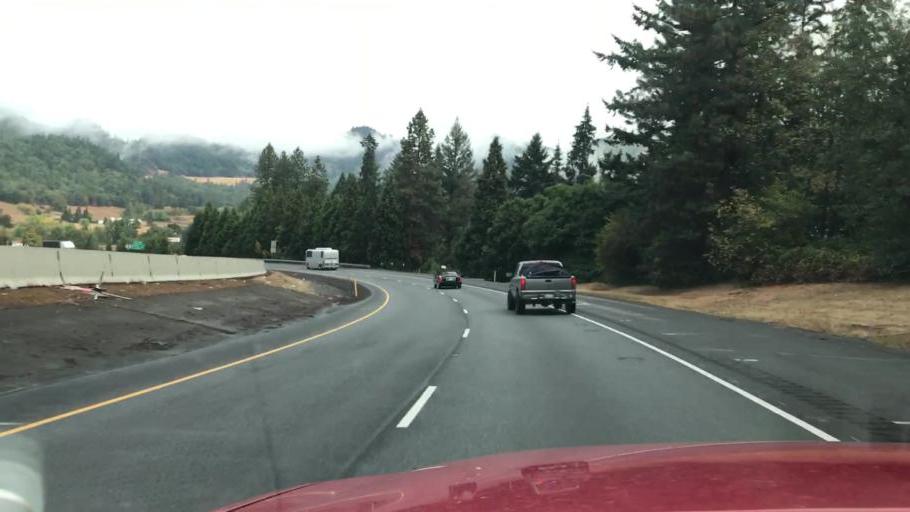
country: US
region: Oregon
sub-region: Josephine County
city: Merlin
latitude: 42.6284
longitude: -123.3802
